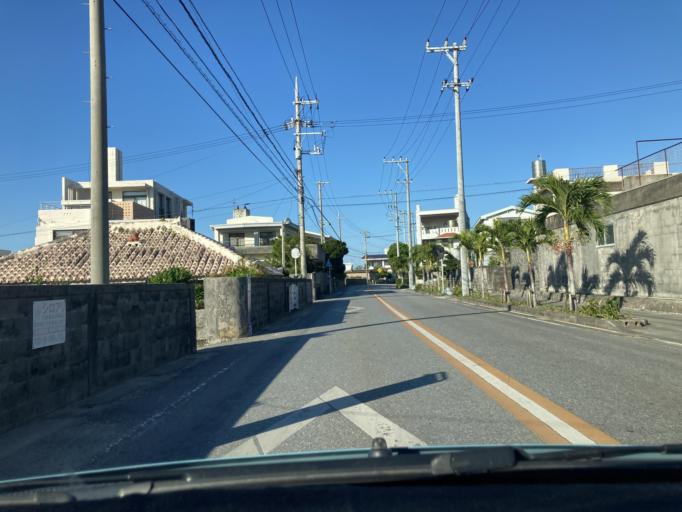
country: JP
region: Okinawa
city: Itoman
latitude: 26.1072
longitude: 127.6650
